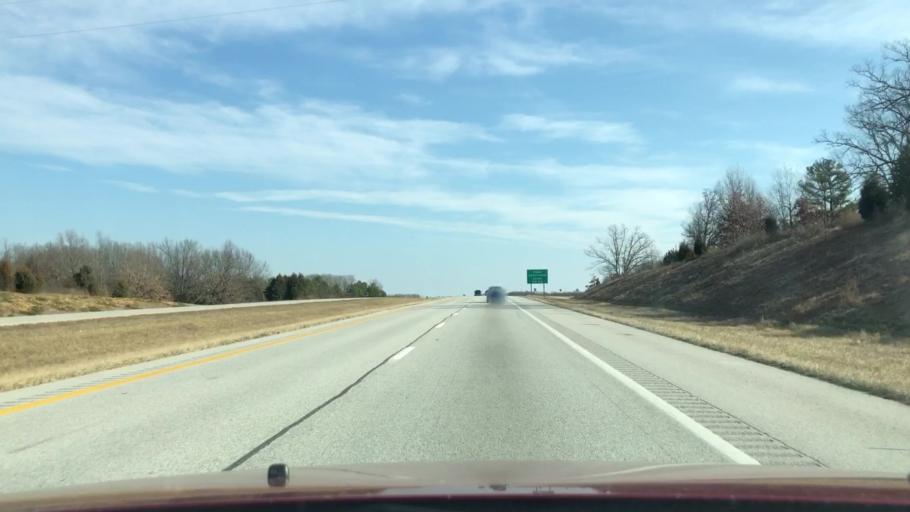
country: US
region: Missouri
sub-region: Webster County
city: Seymour
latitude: 37.1621
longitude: -92.8878
